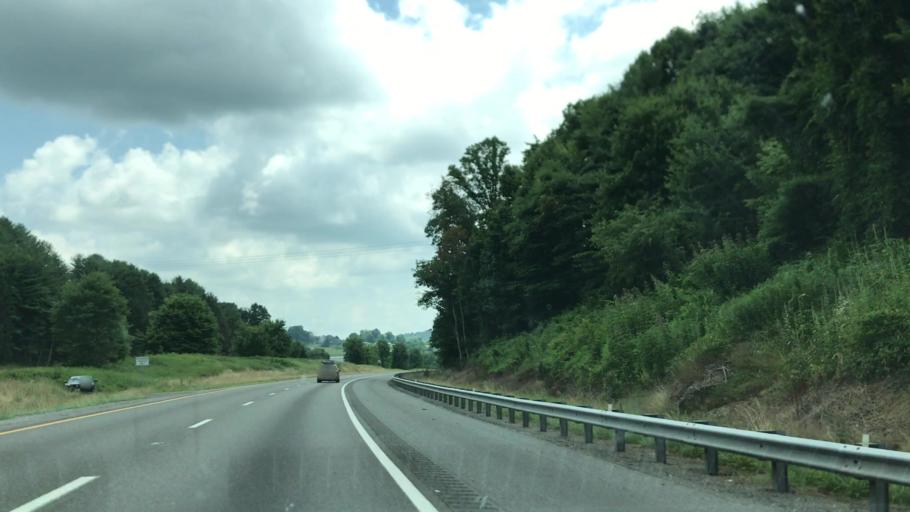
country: US
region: Virginia
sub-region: Carroll County
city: Hillsville
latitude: 36.7523
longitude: -80.7768
